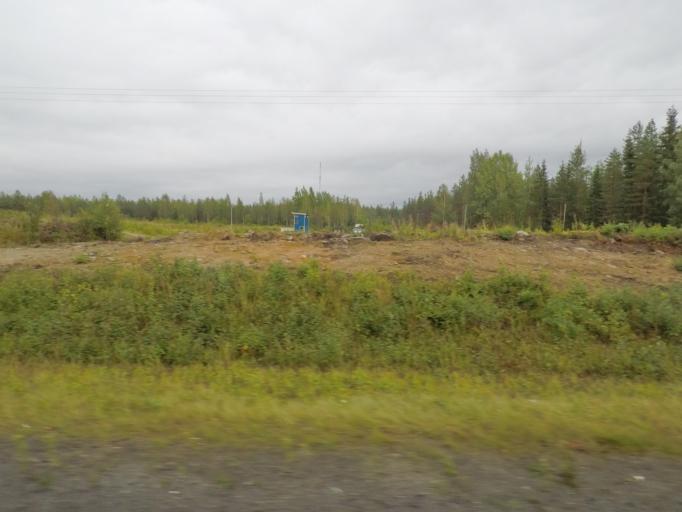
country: FI
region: Southern Savonia
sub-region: Pieksaemaeki
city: Juva
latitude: 61.9533
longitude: 27.8055
